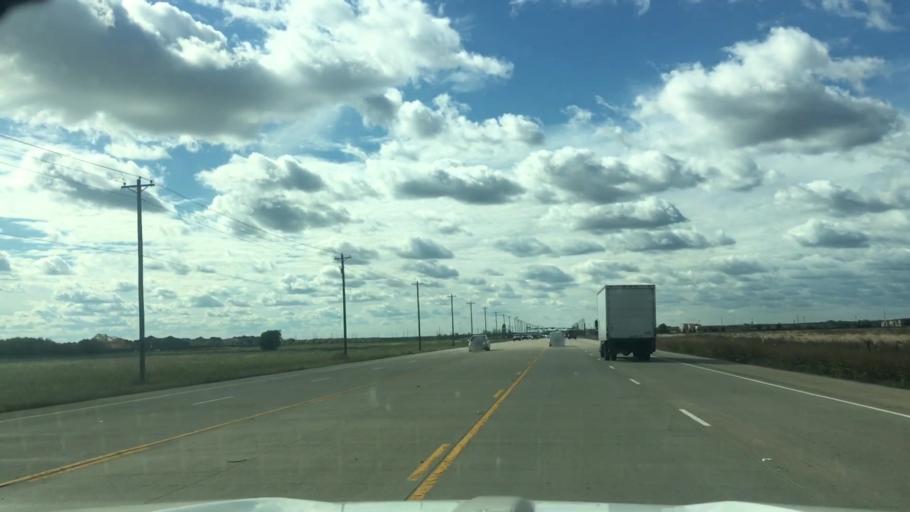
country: US
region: Texas
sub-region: Collin County
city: Prosper
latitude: 33.2192
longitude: -96.8657
